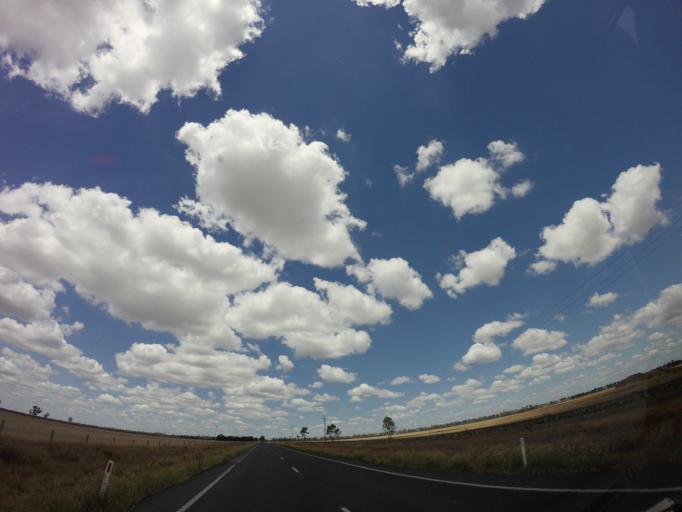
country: AU
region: Queensland
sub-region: Toowoomba
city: Oakey
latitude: -27.8594
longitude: 151.3099
